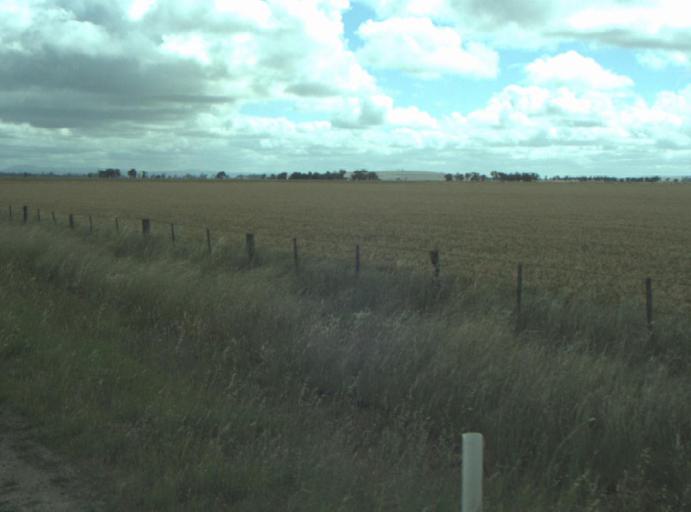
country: AU
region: Victoria
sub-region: Moorabool
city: Bacchus Marsh
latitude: -37.8369
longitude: 144.3561
